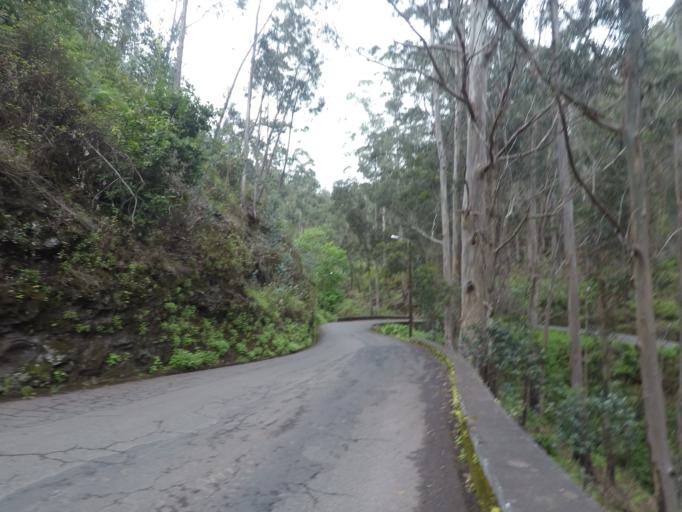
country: PT
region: Madeira
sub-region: Calheta
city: Estreito da Calheta
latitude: 32.7555
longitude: -17.1961
